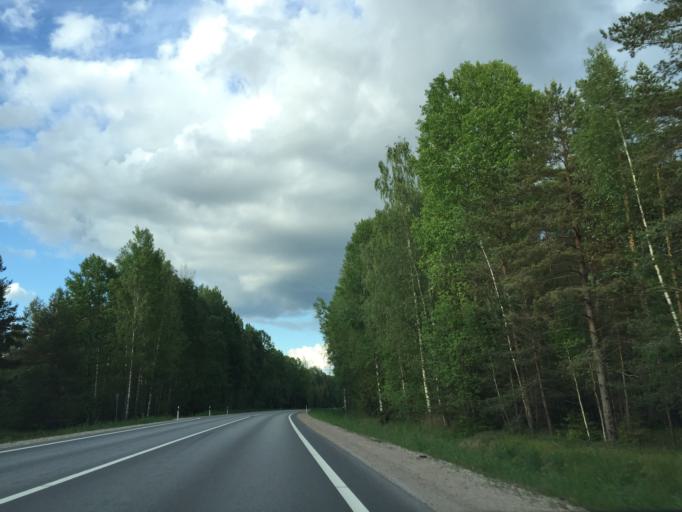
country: LV
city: Tireli
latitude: 56.8098
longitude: 23.4794
